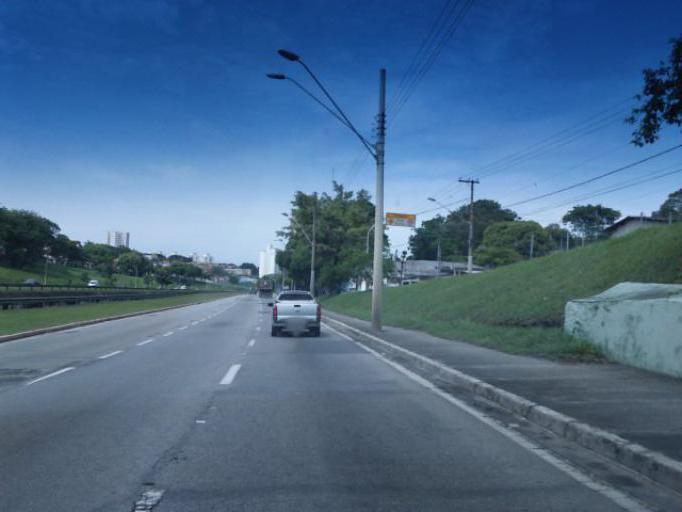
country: BR
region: Sao Paulo
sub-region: Sao Jose Dos Campos
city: Sao Jose dos Campos
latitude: -23.1816
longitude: -45.8774
